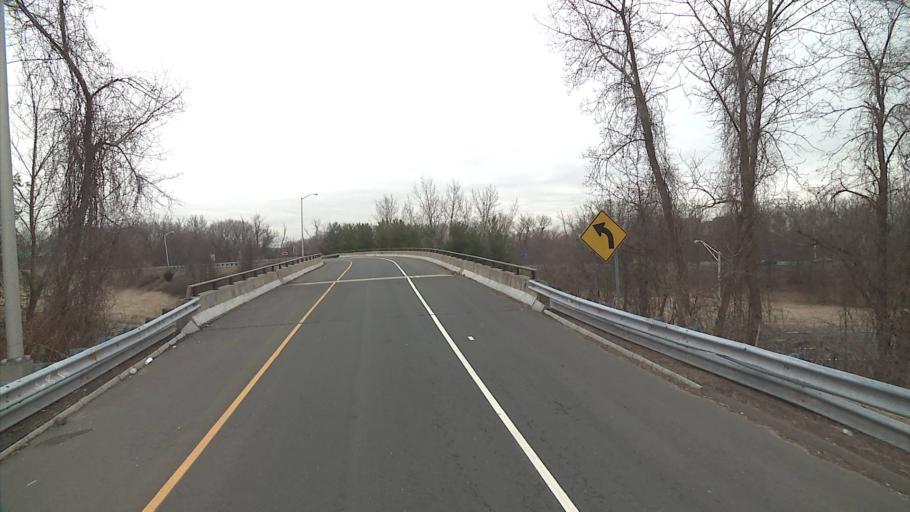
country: US
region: Connecticut
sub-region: Hartford County
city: Hartford
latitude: 41.7546
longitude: -72.6469
